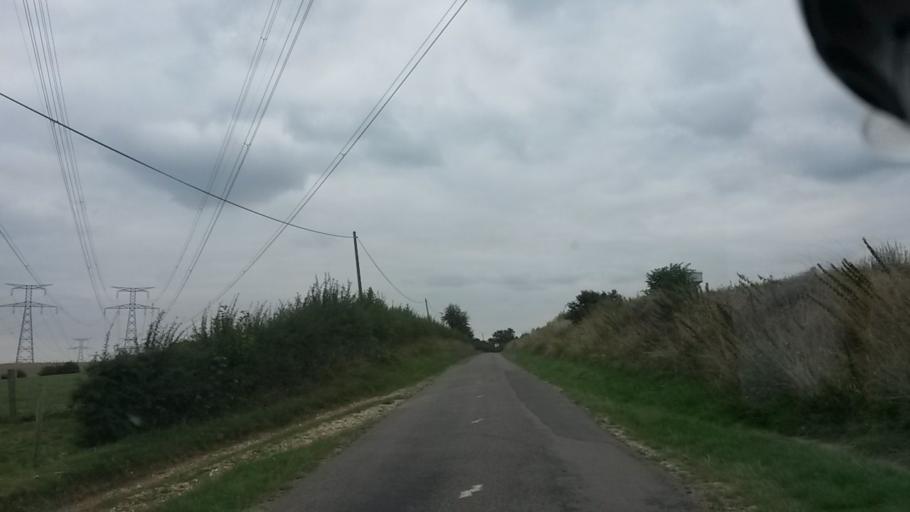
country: FR
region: Haute-Normandie
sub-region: Departement de la Seine-Maritime
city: La Feuillie
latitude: 49.4762
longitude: 1.5291
